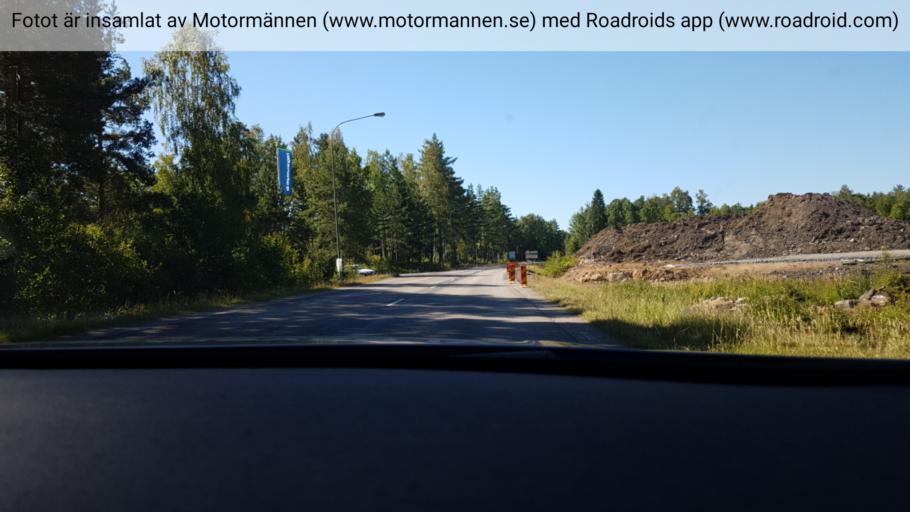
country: SE
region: Vaestra Goetaland
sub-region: Tidaholms Kommun
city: Tidaholm
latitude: 58.1662
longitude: 13.9634
